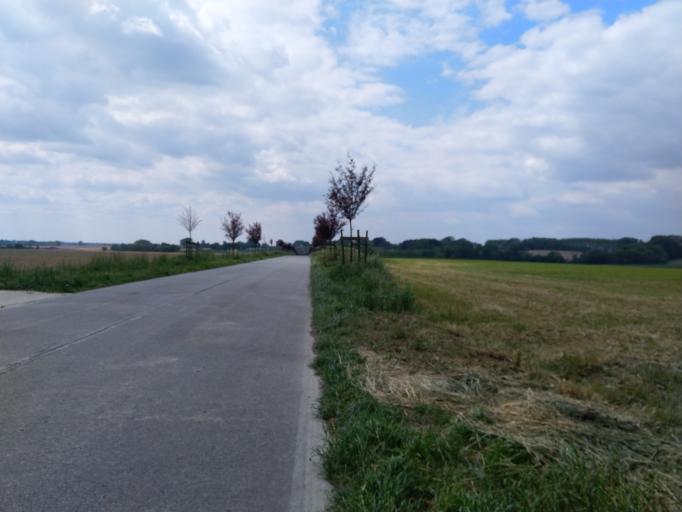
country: BE
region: Wallonia
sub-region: Province du Hainaut
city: Silly
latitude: 50.6180
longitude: 3.9681
